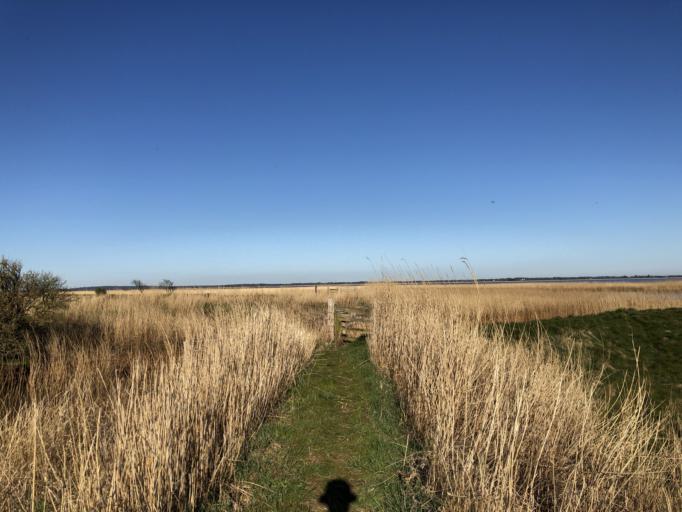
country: DK
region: Central Jutland
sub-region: Holstebro Kommune
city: Ulfborg
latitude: 56.2963
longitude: 8.2763
